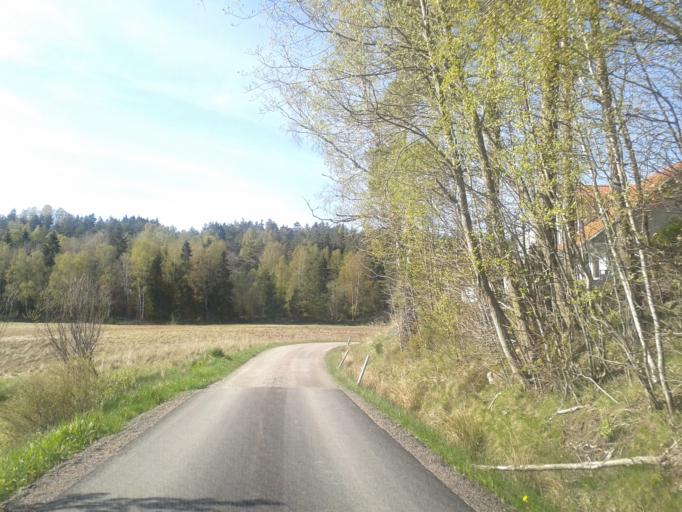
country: SE
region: Vaestra Goetaland
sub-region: Ale Kommun
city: Nodinge-Nol
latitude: 57.8946
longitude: 12.0811
